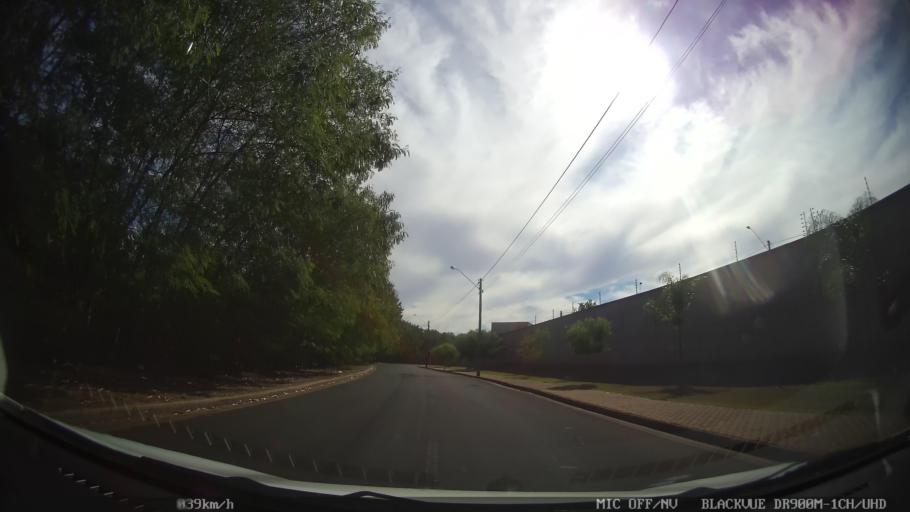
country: BR
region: Sao Paulo
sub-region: Catanduva
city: Catanduva
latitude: -21.1246
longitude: -48.9602
